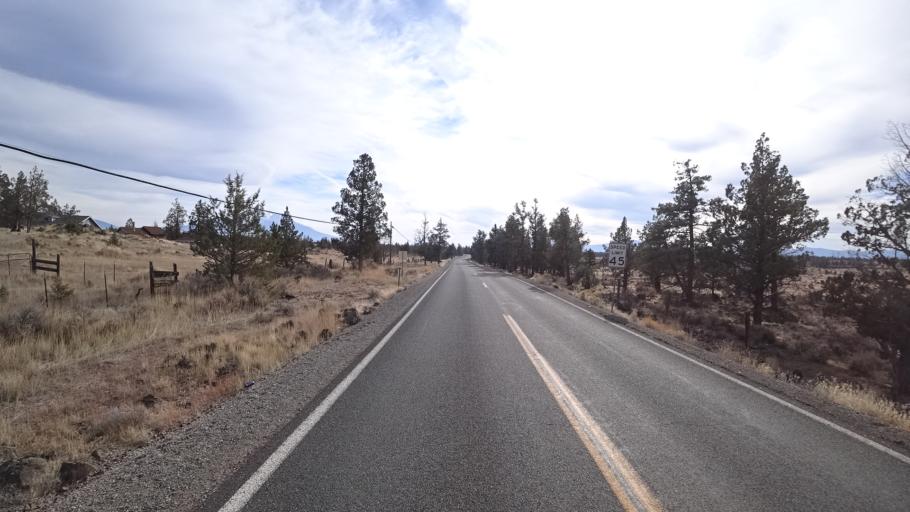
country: US
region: California
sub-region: Siskiyou County
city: Montague
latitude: 41.6584
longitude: -122.3995
